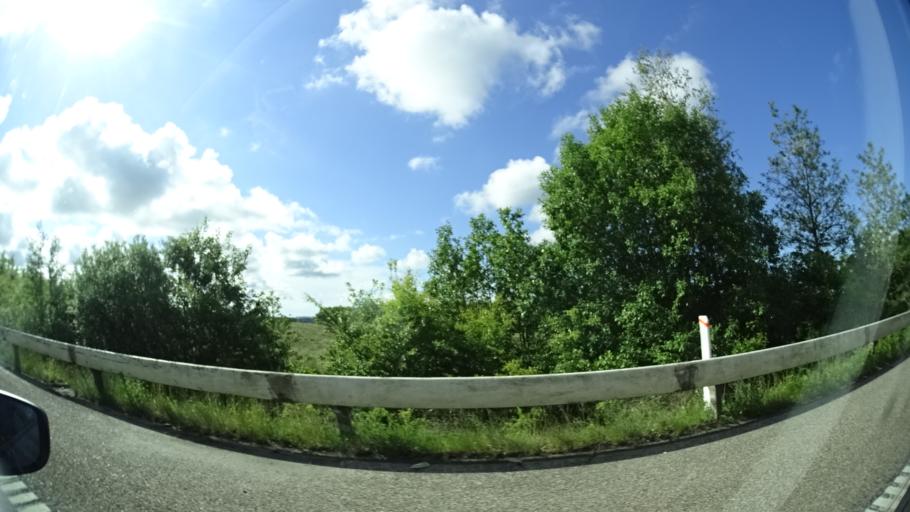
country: DK
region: Central Jutland
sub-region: Syddjurs Kommune
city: Ronde
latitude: 56.3170
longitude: 10.4470
